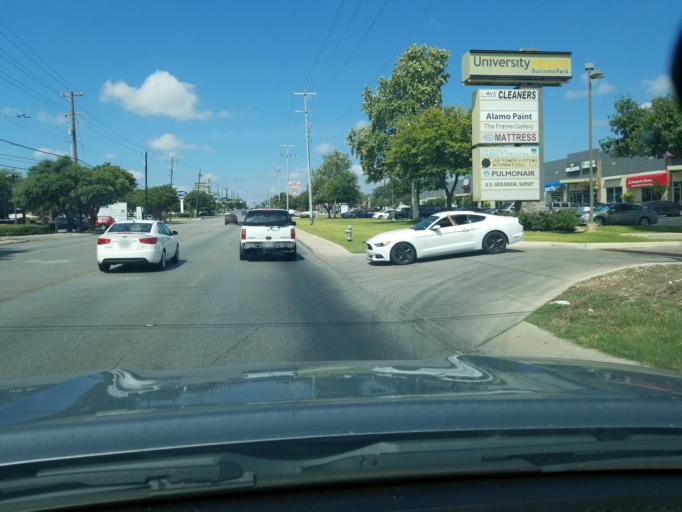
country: US
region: Texas
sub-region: Bexar County
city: Shavano Park
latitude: 29.5632
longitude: -98.5969
